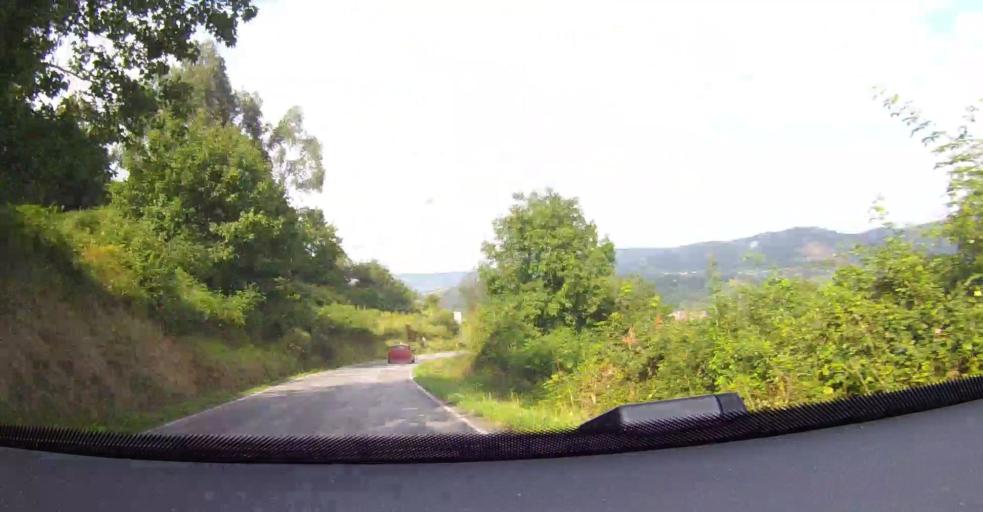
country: ES
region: Asturias
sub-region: Province of Asturias
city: Villaviciosa
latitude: 43.4818
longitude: -5.4261
